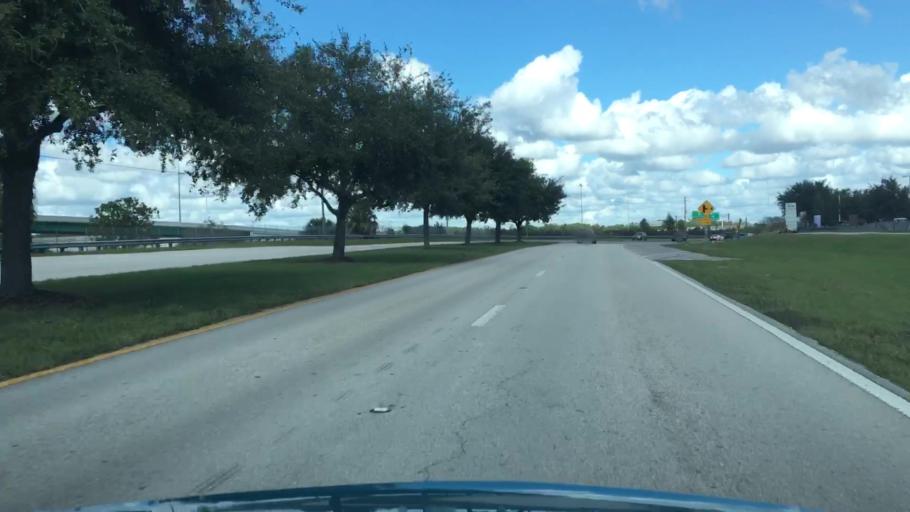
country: US
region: Florida
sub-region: Seminole County
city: Heathrow
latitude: 28.7883
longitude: -81.3472
